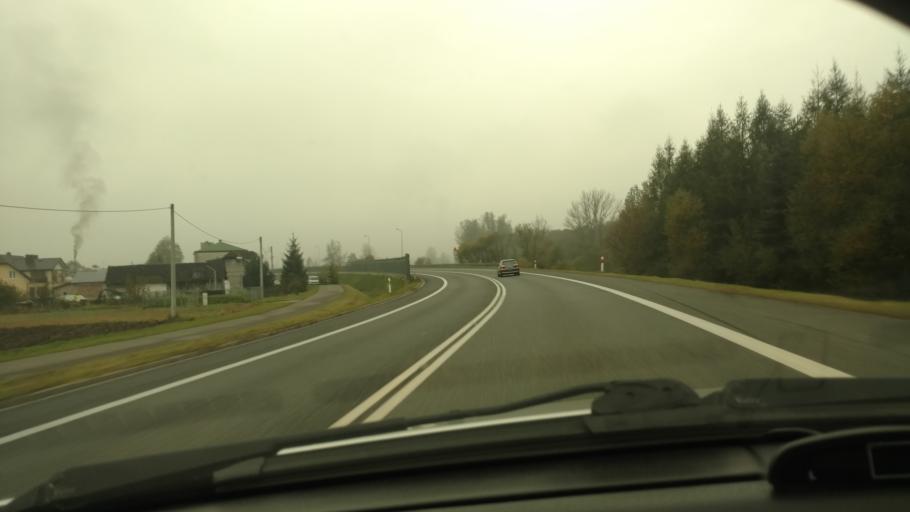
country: PL
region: Lesser Poland Voivodeship
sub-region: Powiat gorlicki
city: Biecz
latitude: 49.7105
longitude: 21.2423
